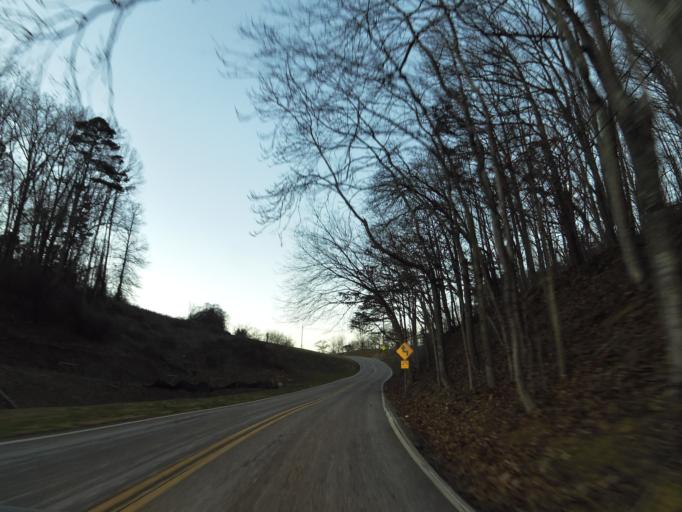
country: US
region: Tennessee
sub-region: Knox County
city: Knoxville
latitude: 35.9882
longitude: -83.9644
